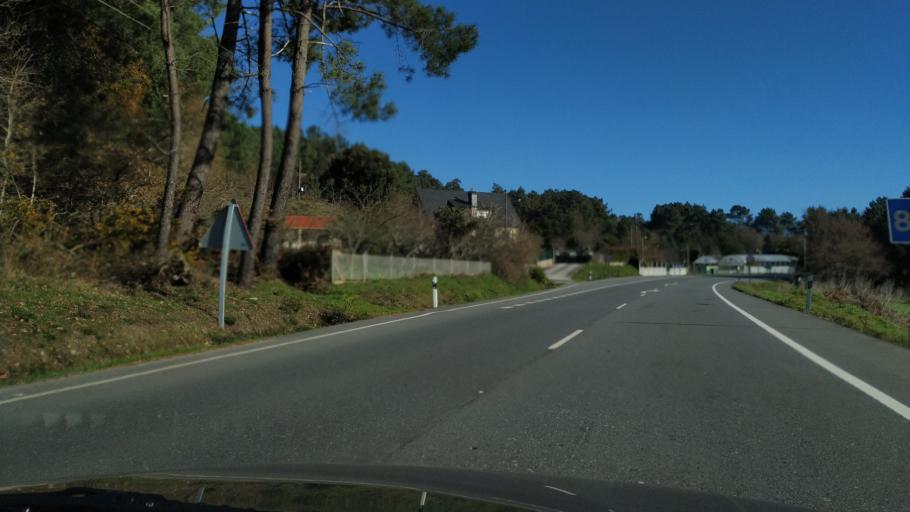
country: ES
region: Galicia
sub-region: Provincia da Coruna
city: Ribeira
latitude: 42.7559
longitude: -8.3679
